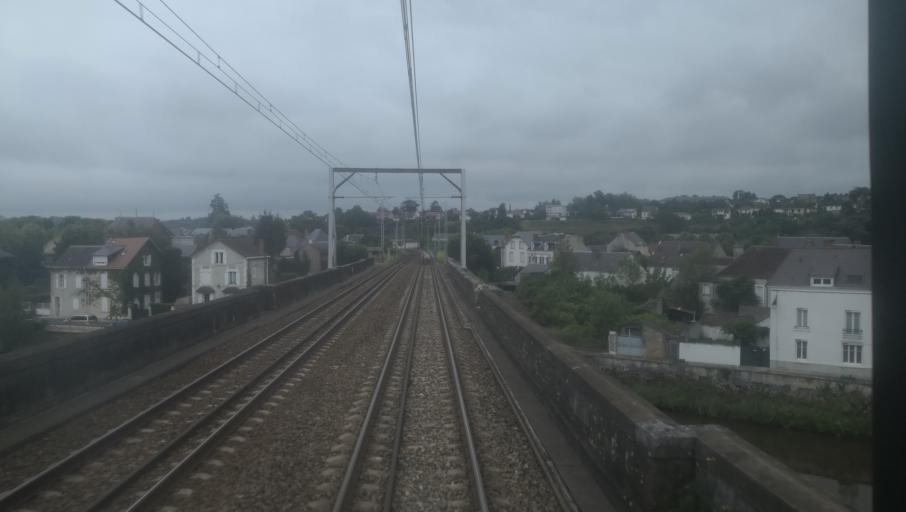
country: FR
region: Centre
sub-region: Departement de l'Indre
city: Argenton-sur-Creuse
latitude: 46.5837
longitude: 1.5249
